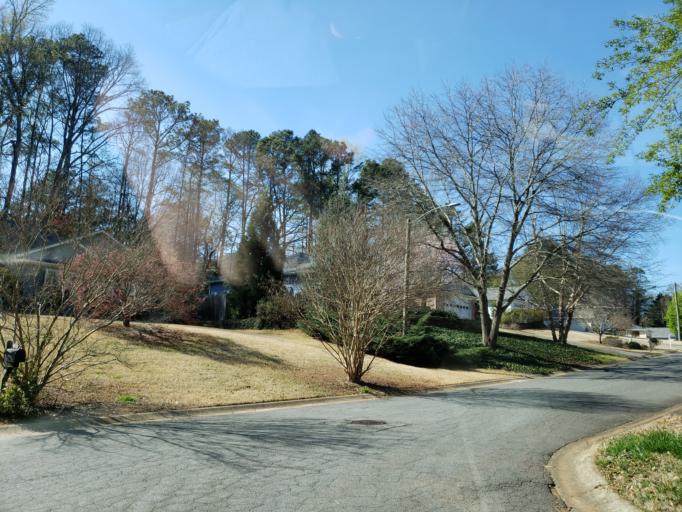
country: US
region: Georgia
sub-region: Cobb County
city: Marietta
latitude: 34.0133
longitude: -84.4839
